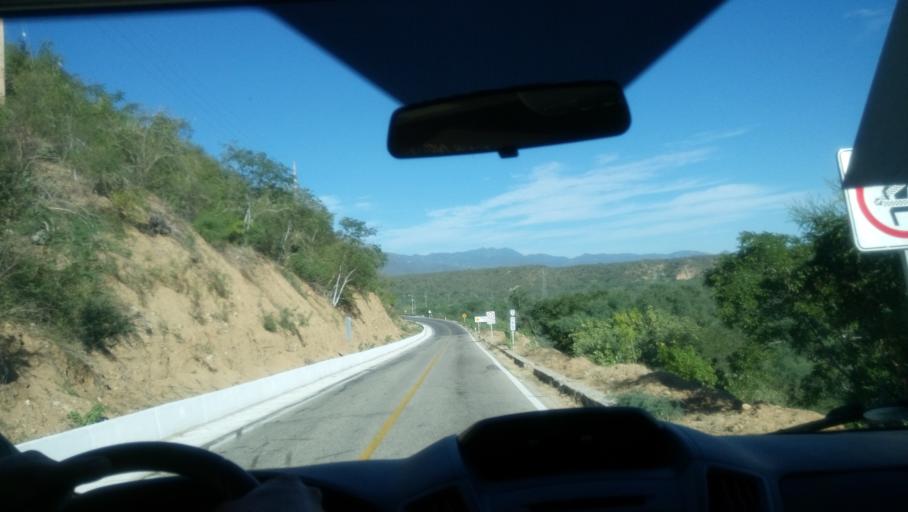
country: MX
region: Baja California Sur
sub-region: Los Cabos
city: Las Veredas
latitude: 23.3291
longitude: -109.7631
